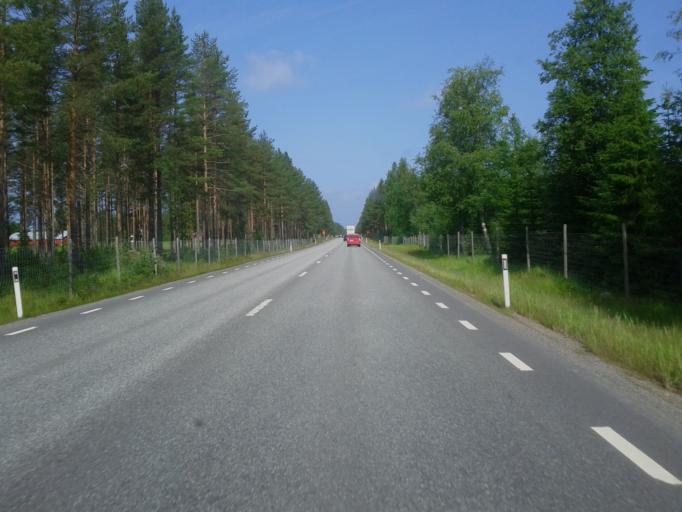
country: SE
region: Vaesterbotten
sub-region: Skelleftea Kommun
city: Burea
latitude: 64.5575
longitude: 21.2391
